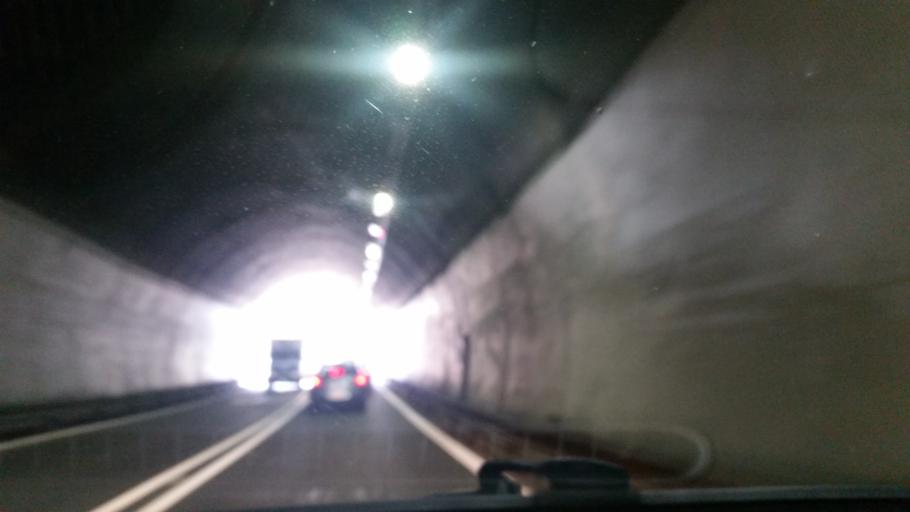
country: IT
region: Campania
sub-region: Provincia di Napoli
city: Napoli
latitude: 40.8568
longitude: 14.2328
